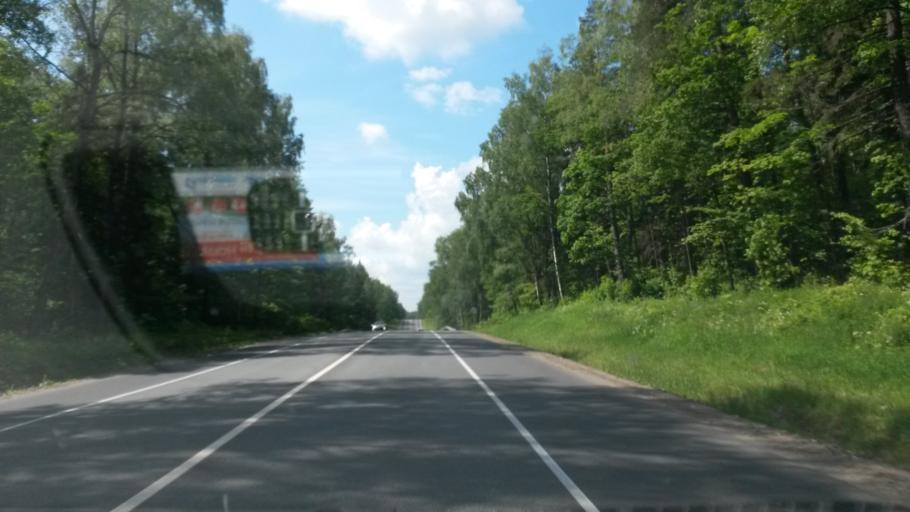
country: RU
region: Jaroslavl
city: Pereslavl'-Zalesskiy
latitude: 56.8611
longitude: 38.9508
